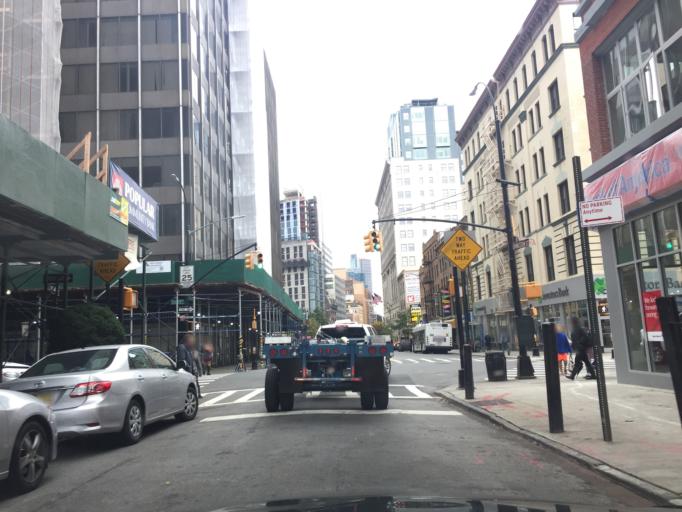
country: US
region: New York
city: New York City
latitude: 40.6917
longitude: -73.9918
